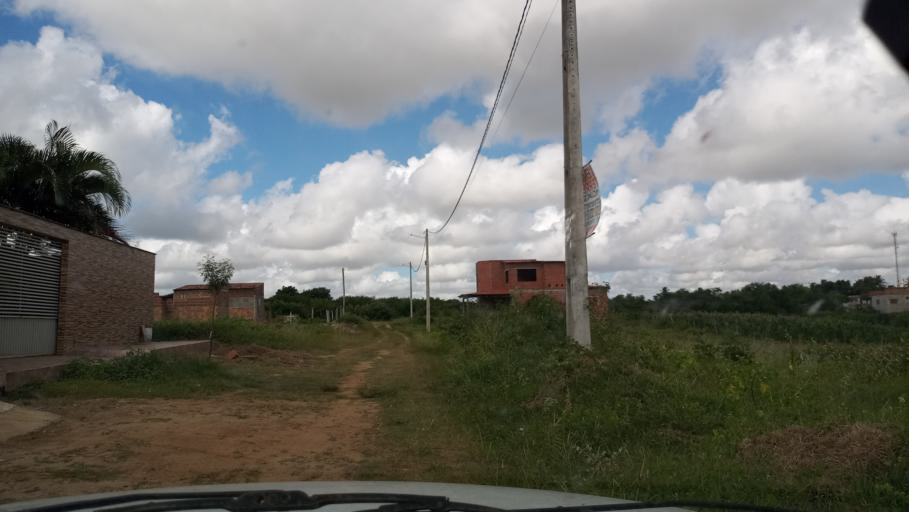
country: BR
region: Rio Grande do Norte
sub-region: Brejinho
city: Brejinho
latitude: -6.1474
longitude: -35.4319
